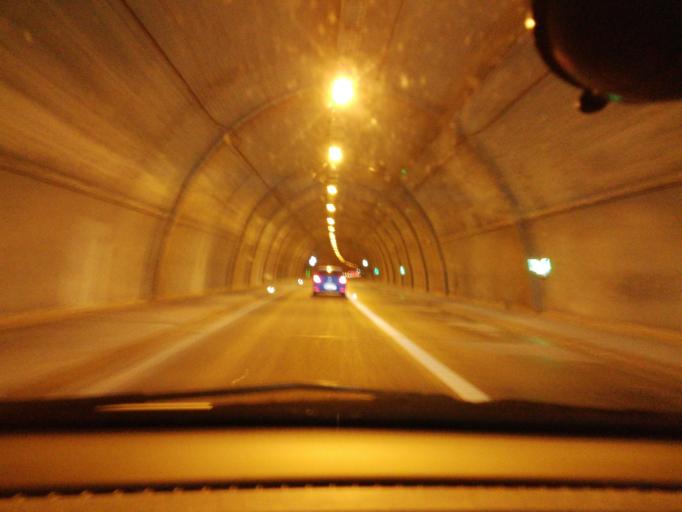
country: DE
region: North Rhine-Westphalia
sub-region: Regierungsbezirk Dusseldorf
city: Wuppertal
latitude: 51.2393
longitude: 7.1279
